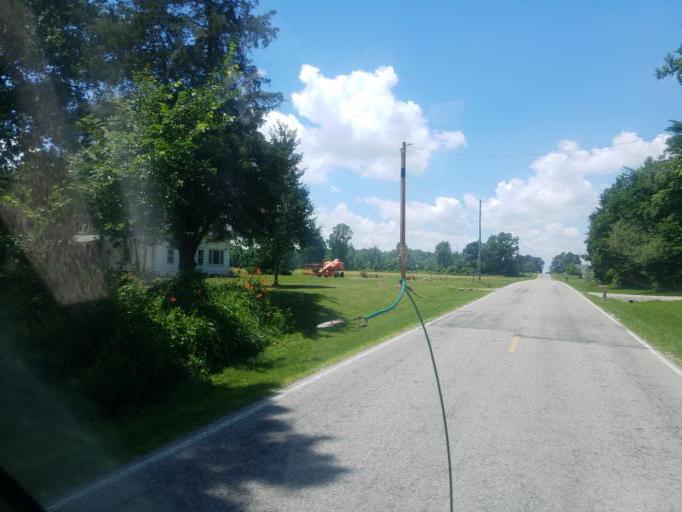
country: US
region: Ohio
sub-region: Huron County
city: Plymouth
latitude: 41.0679
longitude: -82.6269
